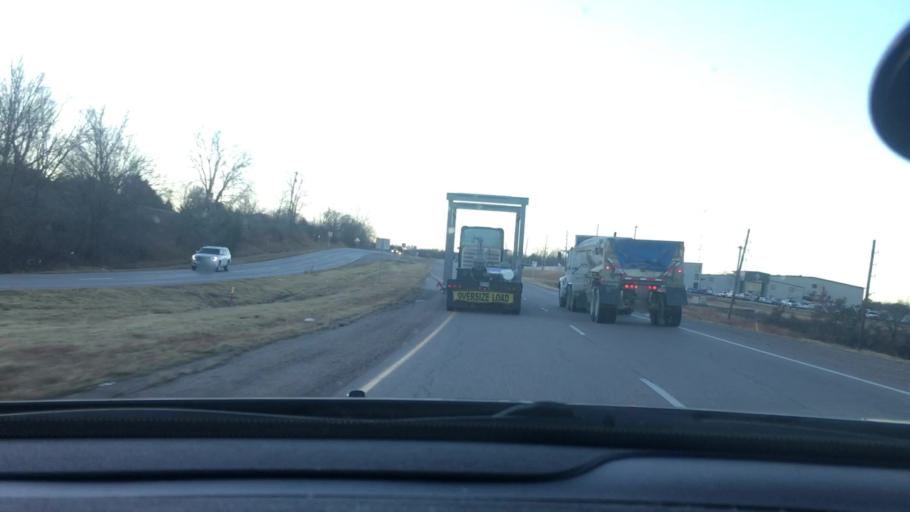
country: US
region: Oklahoma
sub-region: Pontotoc County
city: Ada
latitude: 34.7398
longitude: -96.7093
